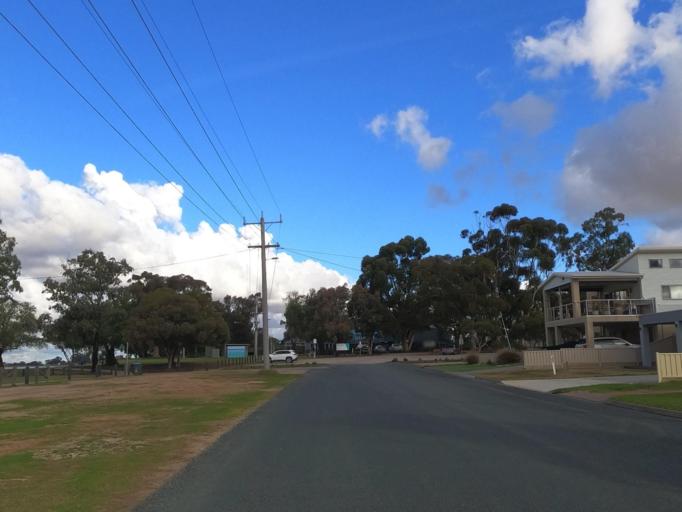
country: AU
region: Victoria
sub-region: Swan Hill
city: Swan Hill
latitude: -35.4493
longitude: 143.6275
